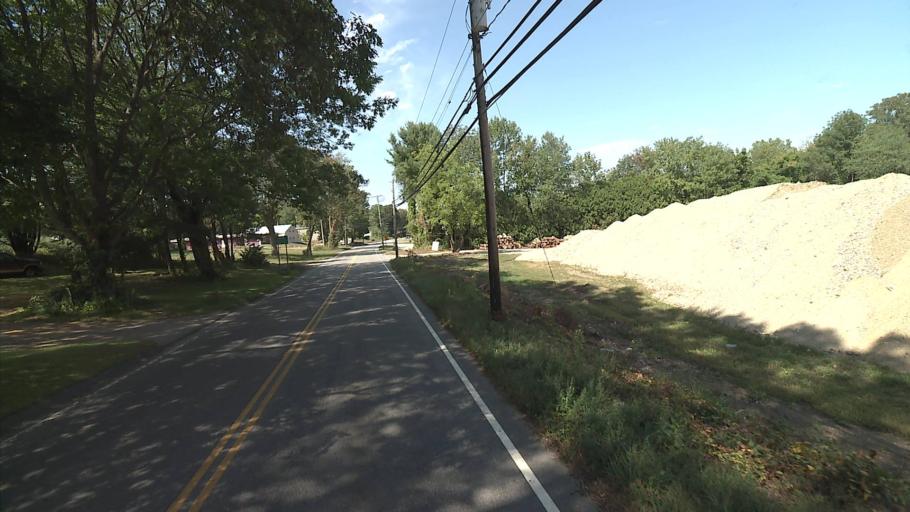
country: US
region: Connecticut
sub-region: New London County
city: Baltic
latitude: 41.5737
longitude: -72.1360
